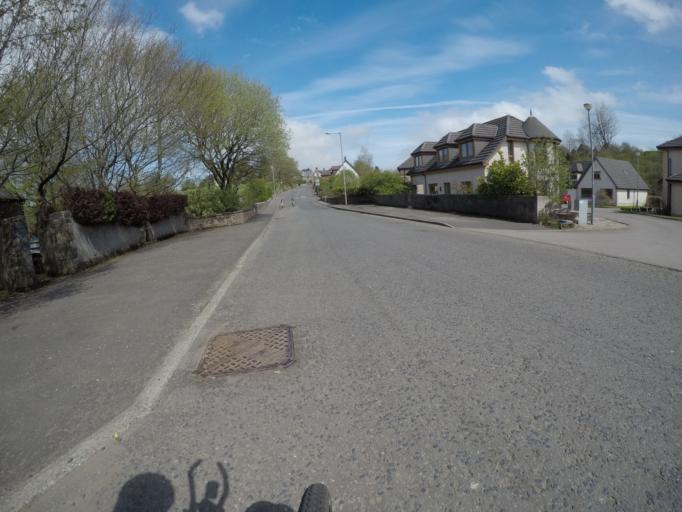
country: GB
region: Scotland
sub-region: East Ayrshire
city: Stewarton
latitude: 55.6851
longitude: -4.5070
